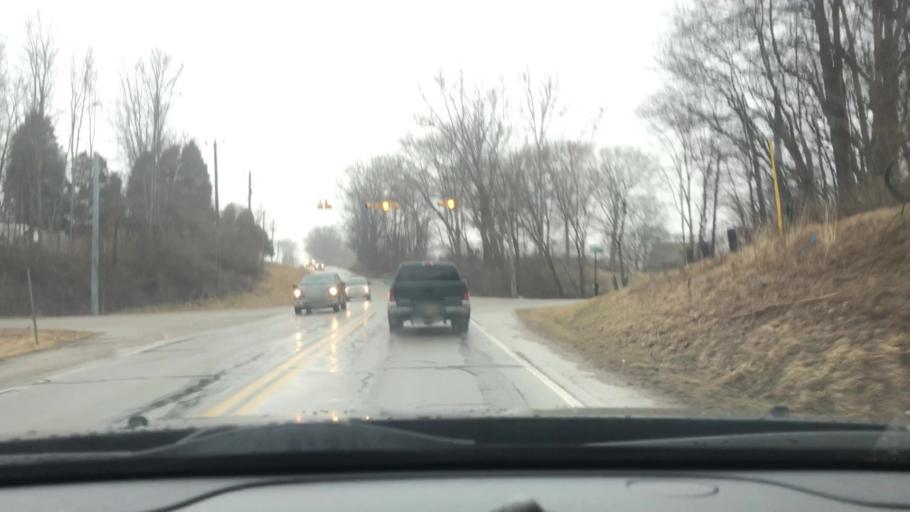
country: US
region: Indiana
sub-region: Morgan County
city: Mooresville
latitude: 39.5939
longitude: -86.3407
